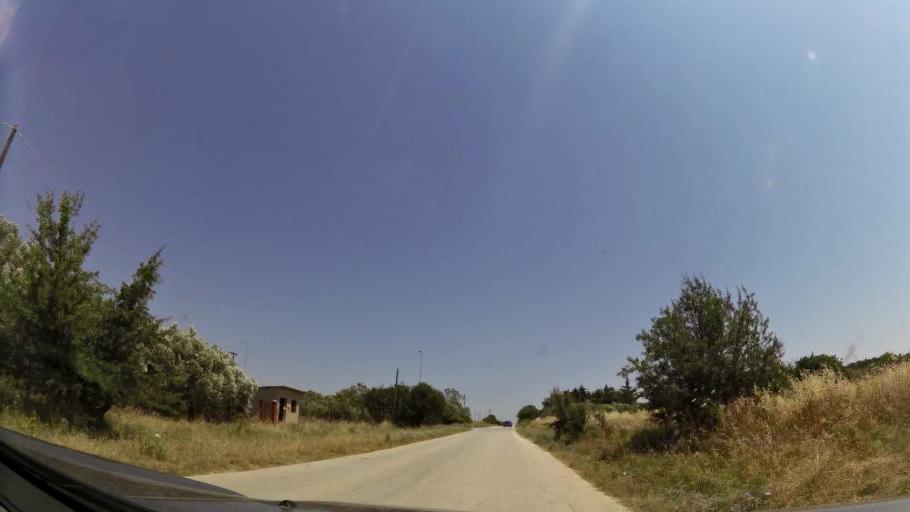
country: GR
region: Central Macedonia
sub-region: Nomos Thessalonikis
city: Nea Michaniona
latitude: 40.4740
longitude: 22.8762
